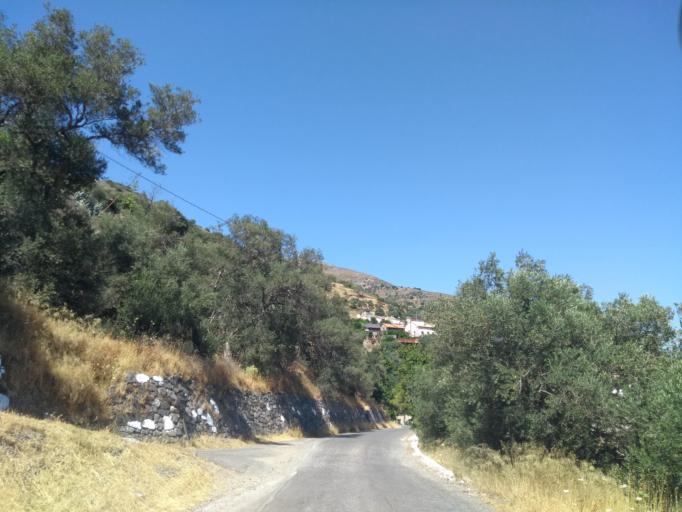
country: GR
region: Crete
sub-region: Nomos Chanias
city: Vryses
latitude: 35.3633
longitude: 23.5957
